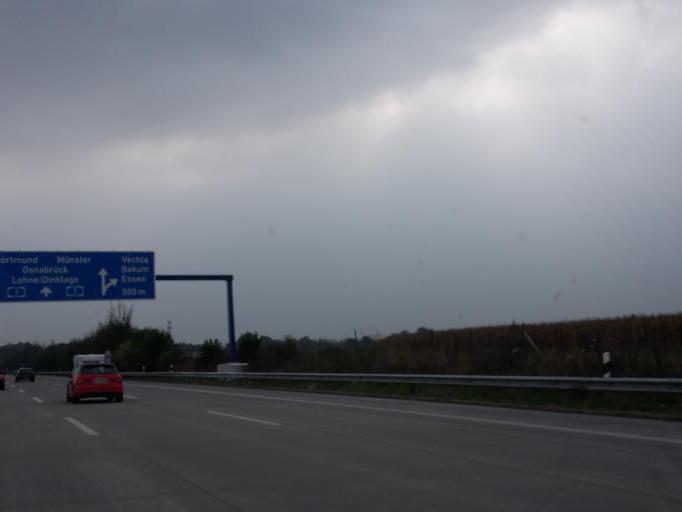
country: DE
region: Lower Saxony
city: Bakum
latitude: 52.7352
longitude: 8.1745
